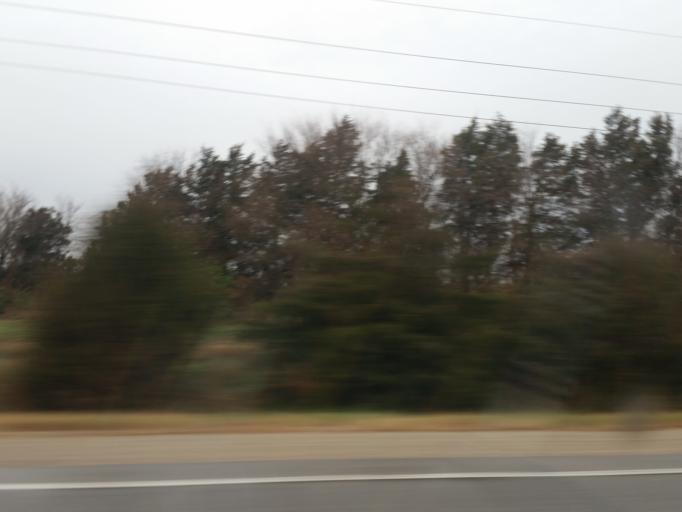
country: US
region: Iowa
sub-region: Black Hawk County
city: Elk Run Heights
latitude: 42.4038
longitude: -92.2602
